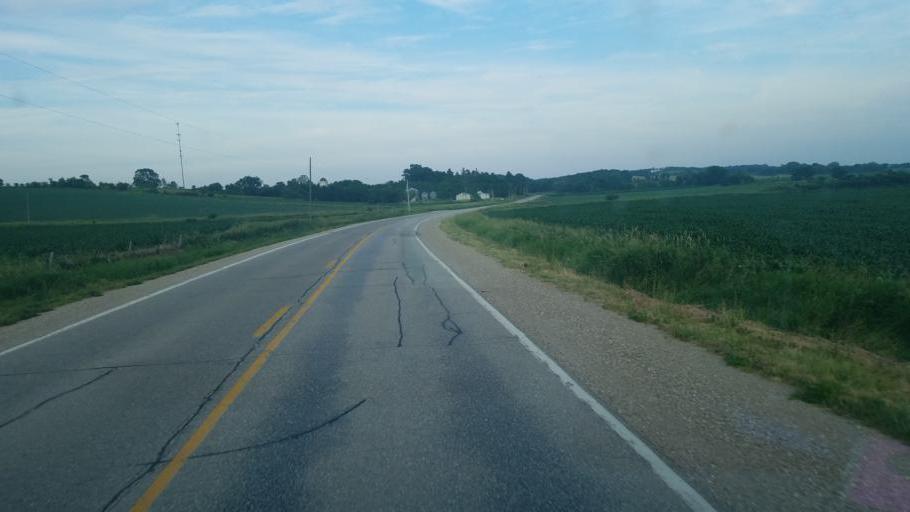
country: US
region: Iowa
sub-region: Tama County
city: Tama
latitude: 41.9608
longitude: -92.4376
